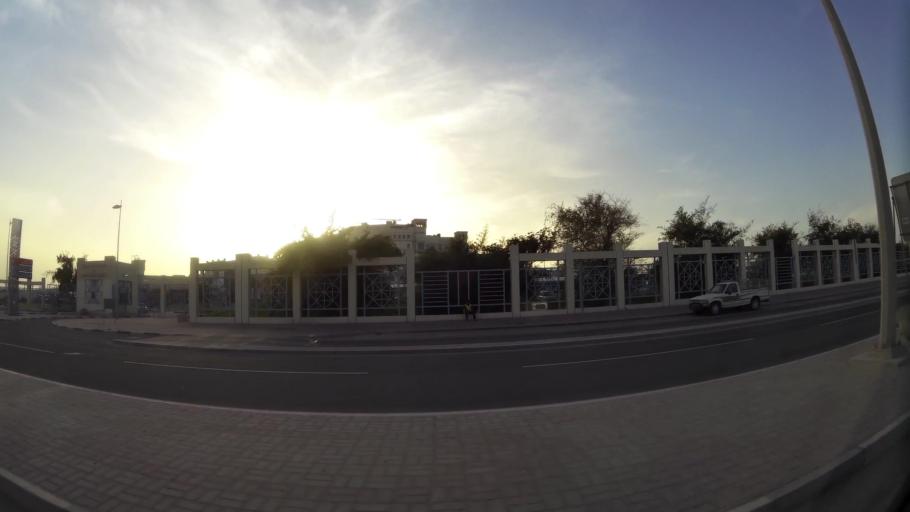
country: QA
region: Al Wakrah
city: Al Wakrah
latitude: 25.1670
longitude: 51.5906
